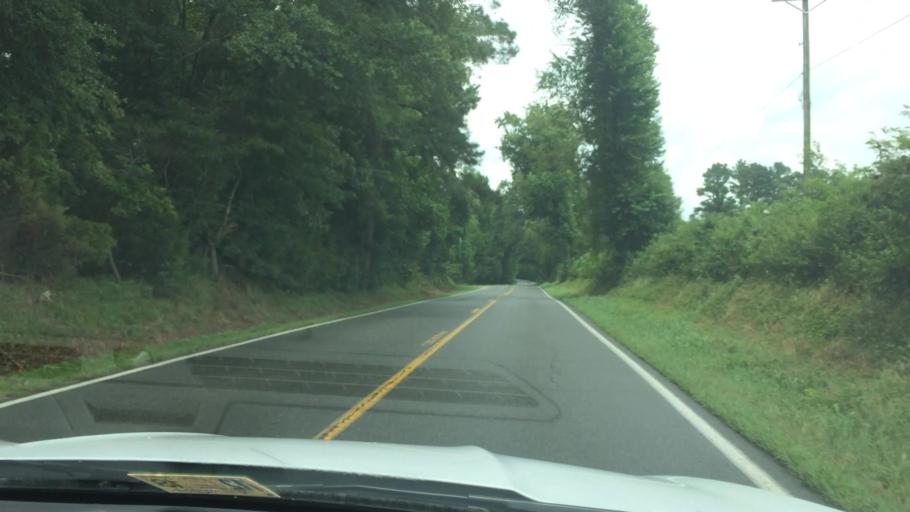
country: US
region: Virginia
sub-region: Charles City County
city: Charles City
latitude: 37.4199
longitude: -77.0416
